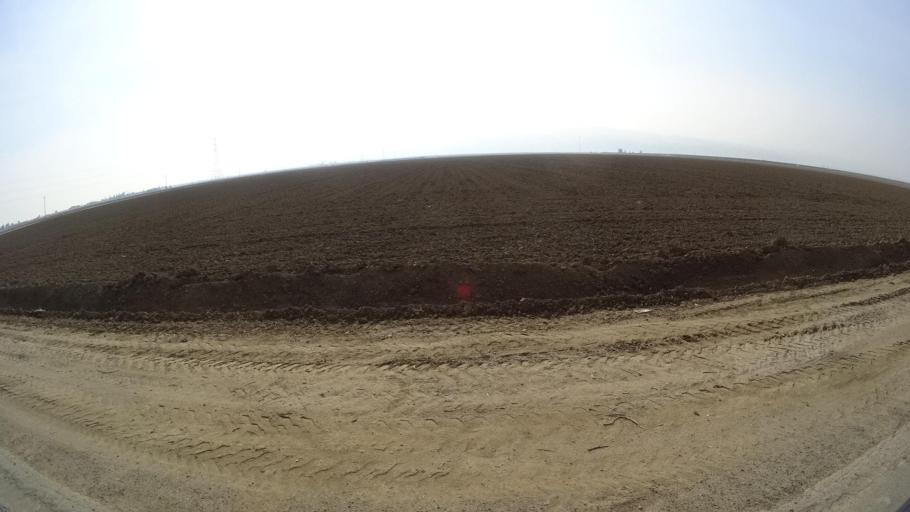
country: US
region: California
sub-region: Kern County
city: Weedpatch
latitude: 35.0762
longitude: -118.9871
